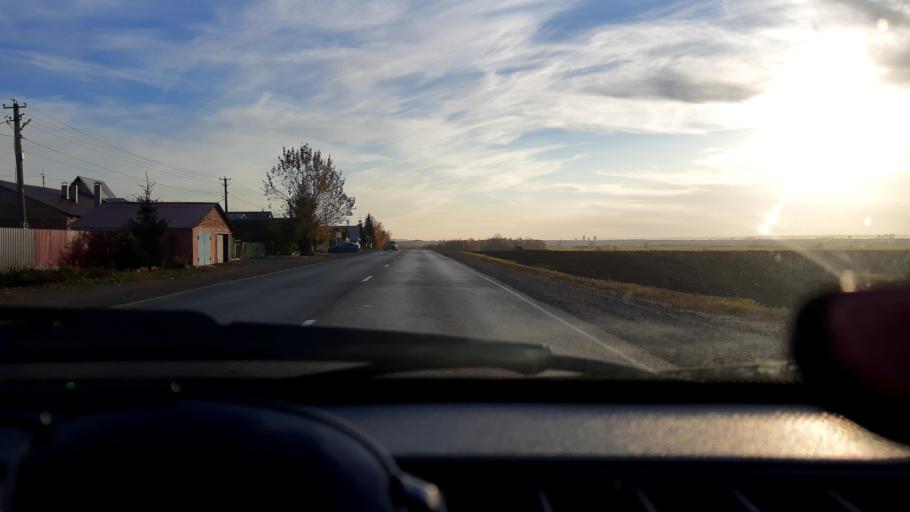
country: RU
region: Bashkortostan
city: Ufa
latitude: 54.8223
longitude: 55.9875
